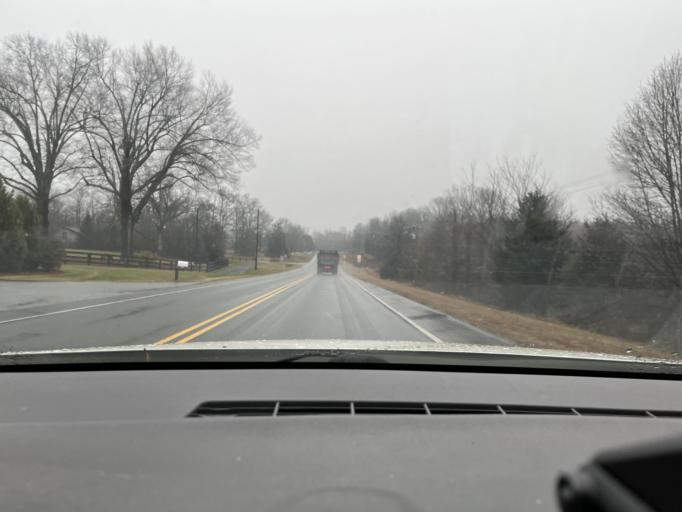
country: US
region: North Carolina
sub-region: Guilford County
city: Pleasant Garden
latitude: 36.0005
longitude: -79.7462
